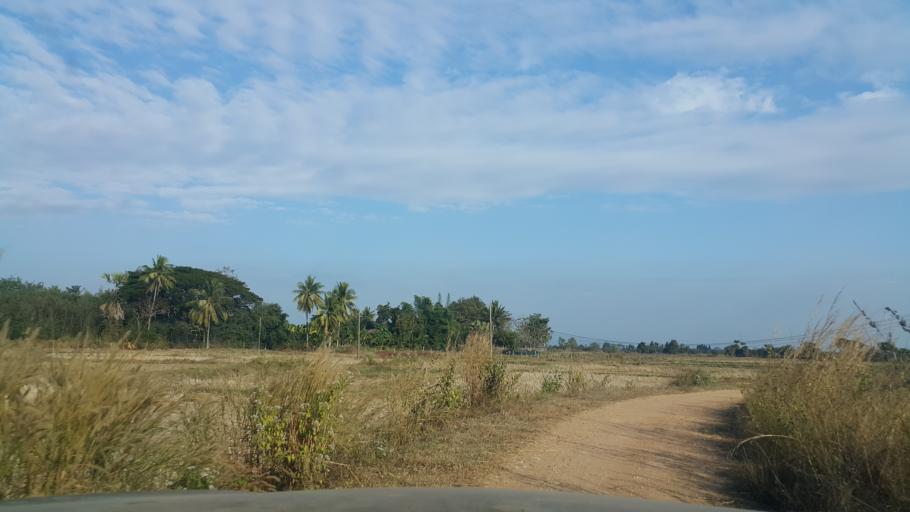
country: TH
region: Lampang
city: Ko Kha
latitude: 18.2260
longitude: 99.3550
